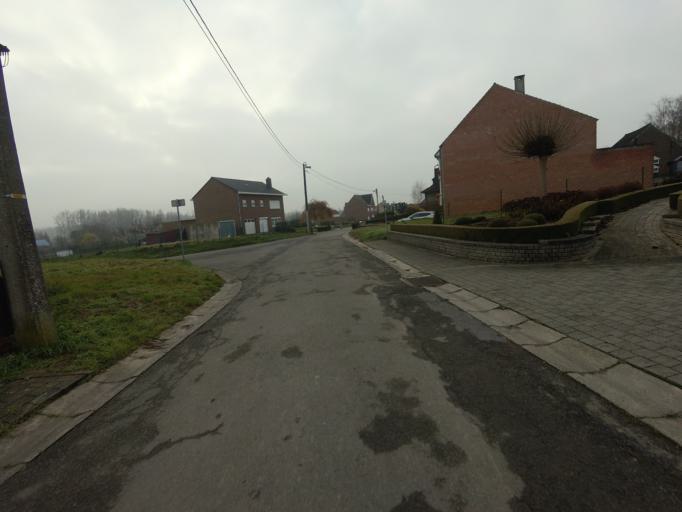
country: BE
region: Flanders
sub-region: Provincie Oost-Vlaanderen
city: Ninove
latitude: 50.8177
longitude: 3.9791
